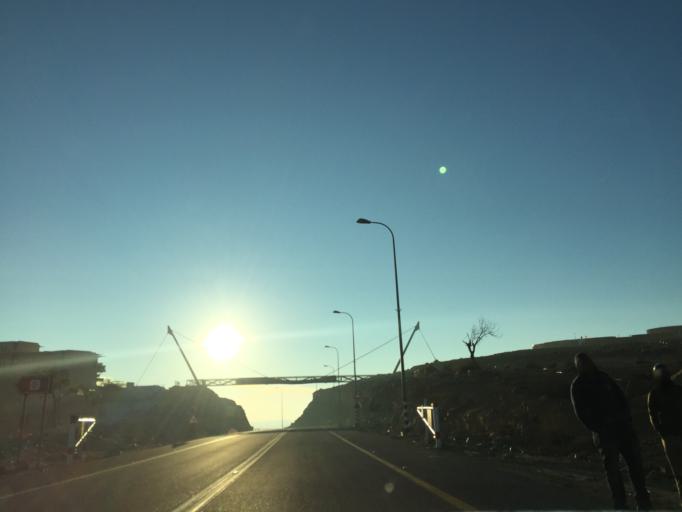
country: IL
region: Southern District
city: Mitzpe Ramon
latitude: 30.6106
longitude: 34.8058
